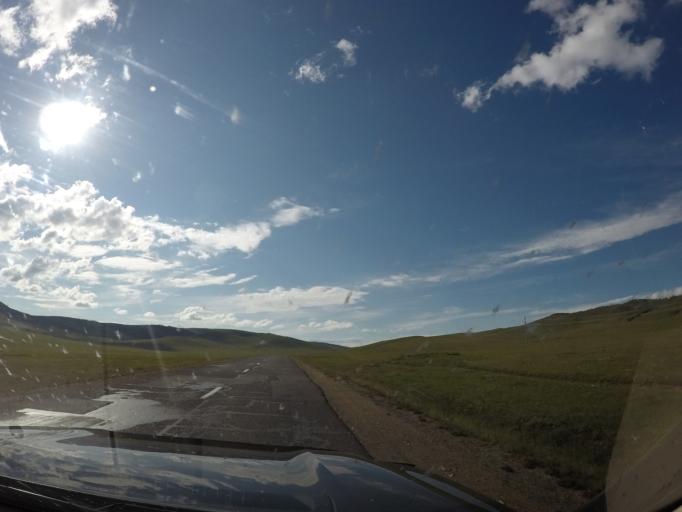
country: MN
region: Hentiy
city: Modot
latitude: 47.7688
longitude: 108.8773
